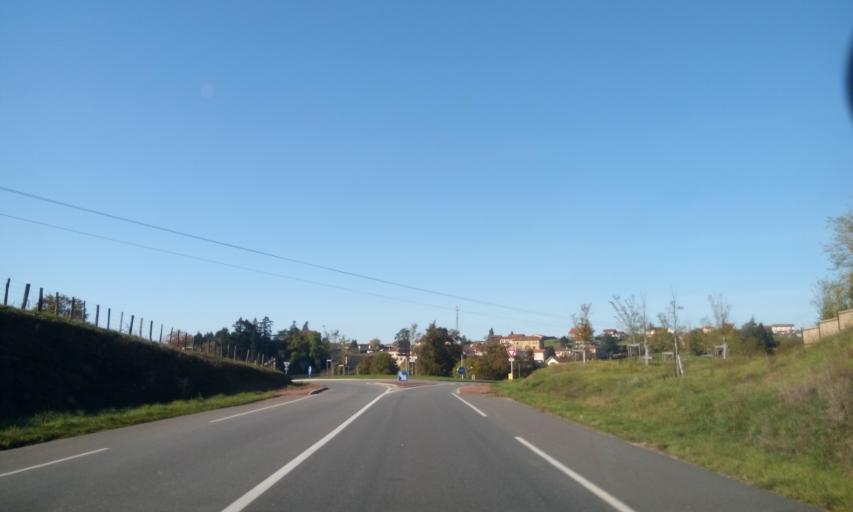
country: FR
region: Rhone-Alpes
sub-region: Departement de la Loire
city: Coutouvre
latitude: 46.0338
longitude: 4.2449
